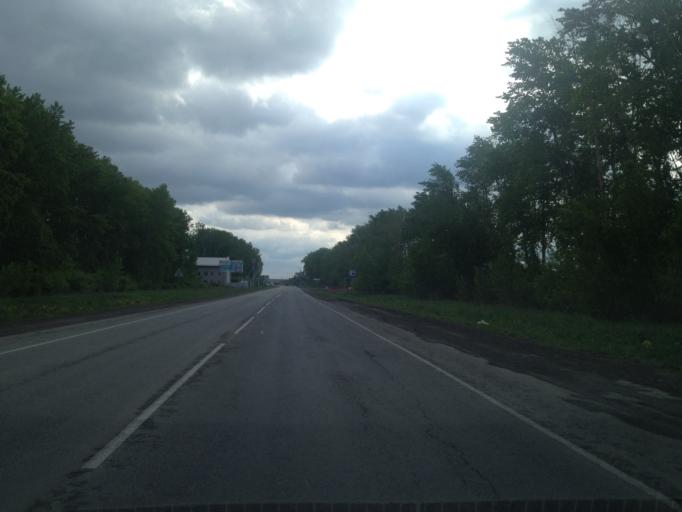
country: RU
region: Sverdlovsk
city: Aramil
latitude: 56.6950
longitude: 60.7812
